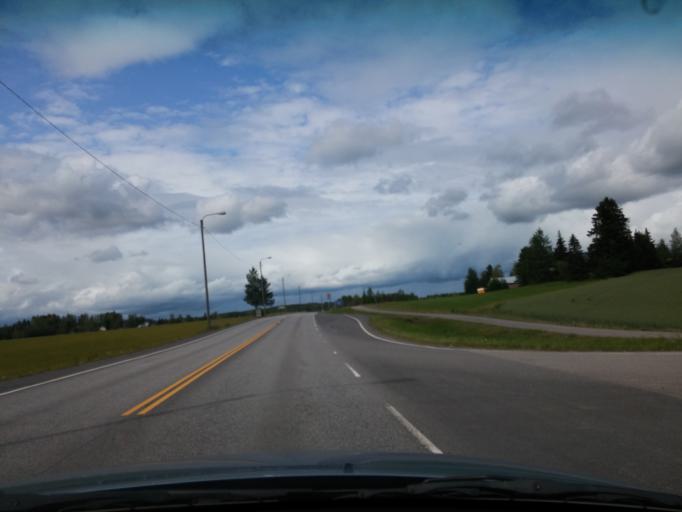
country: FI
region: Uusimaa
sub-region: Porvoo
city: Askola
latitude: 60.5208
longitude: 25.5793
